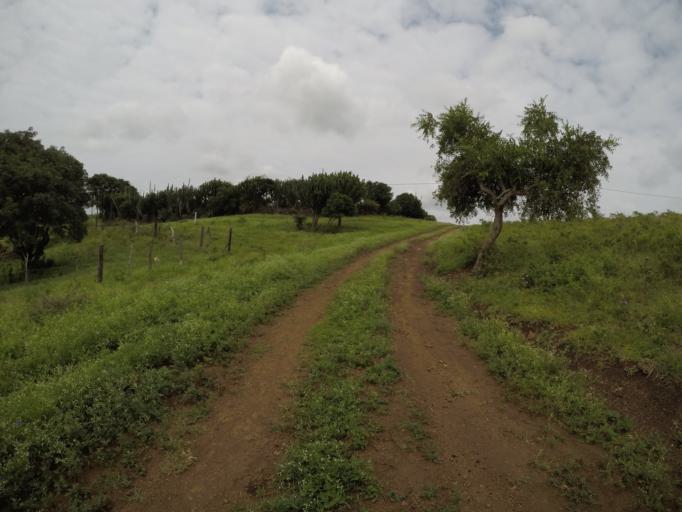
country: ZA
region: KwaZulu-Natal
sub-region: uThungulu District Municipality
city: Empangeni
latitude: -28.6108
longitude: 31.9000
